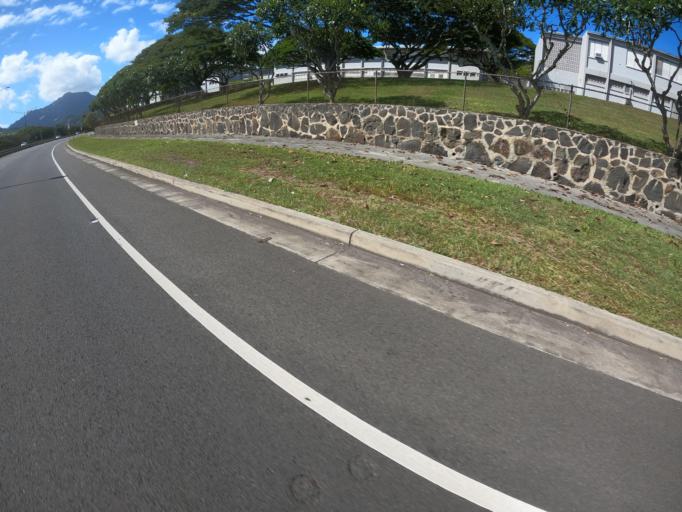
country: US
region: Hawaii
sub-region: Honolulu County
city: Kailua
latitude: 21.4083
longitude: -157.7566
